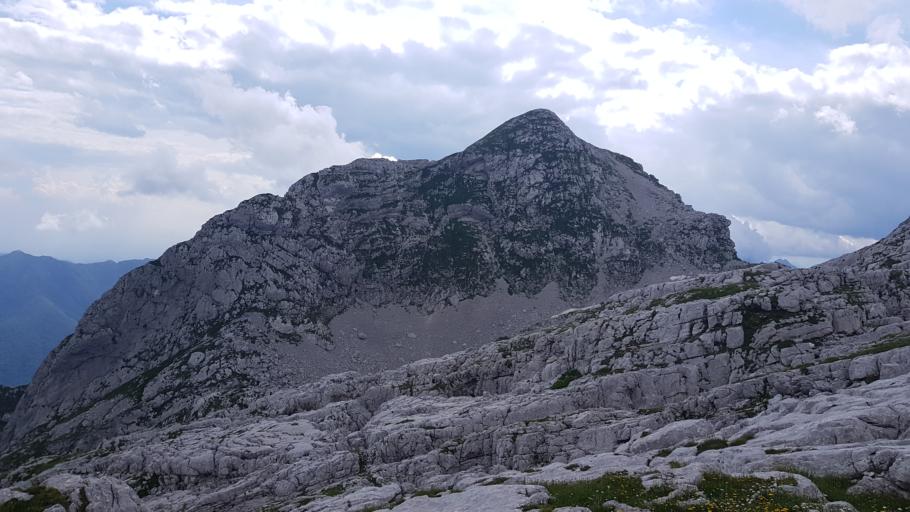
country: SI
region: Bovec
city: Bovec
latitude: 46.3346
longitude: 13.4568
